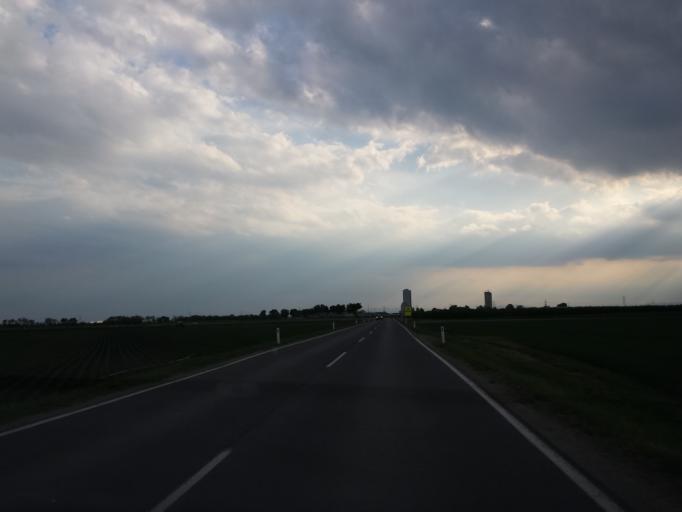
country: AT
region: Lower Austria
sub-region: Politischer Bezirk Ganserndorf
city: Grosshofen
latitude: 48.2467
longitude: 16.6005
